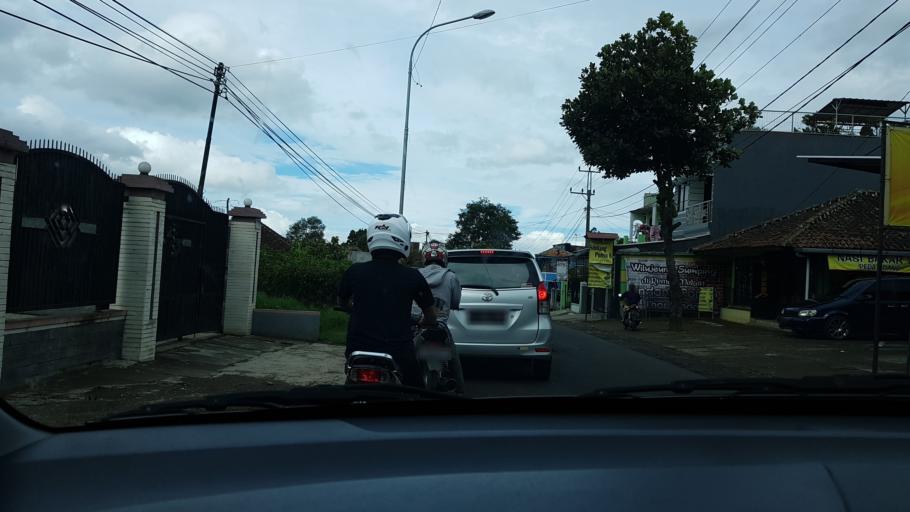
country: ID
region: West Java
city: Banjar
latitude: -7.1114
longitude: 107.4501
